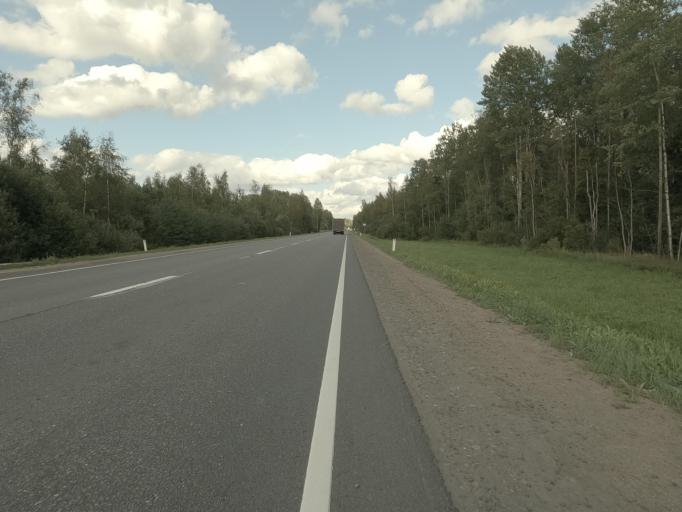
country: RU
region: Leningrad
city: Nikol'skoye
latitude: 59.6599
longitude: 30.8707
